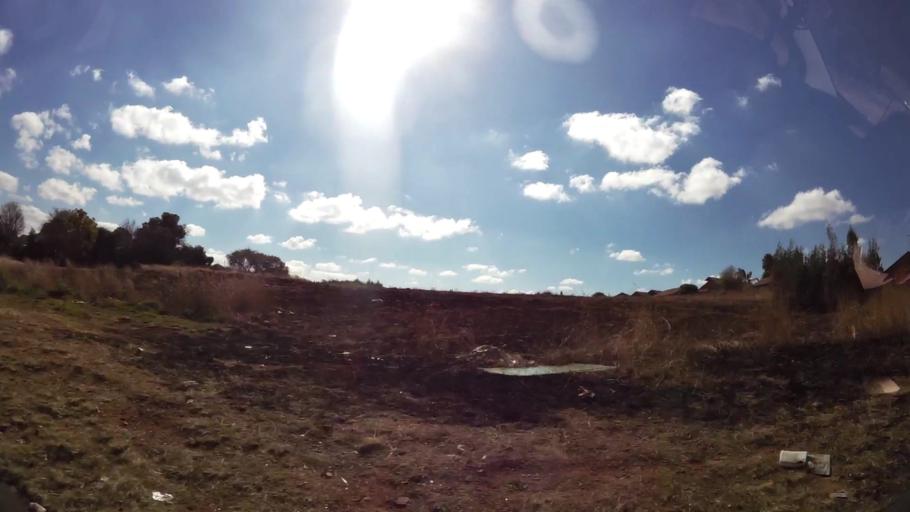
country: ZA
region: Gauteng
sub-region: City of Johannesburg Metropolitan Municipality
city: Roodepoort
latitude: -26.1242
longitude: 27.8414
